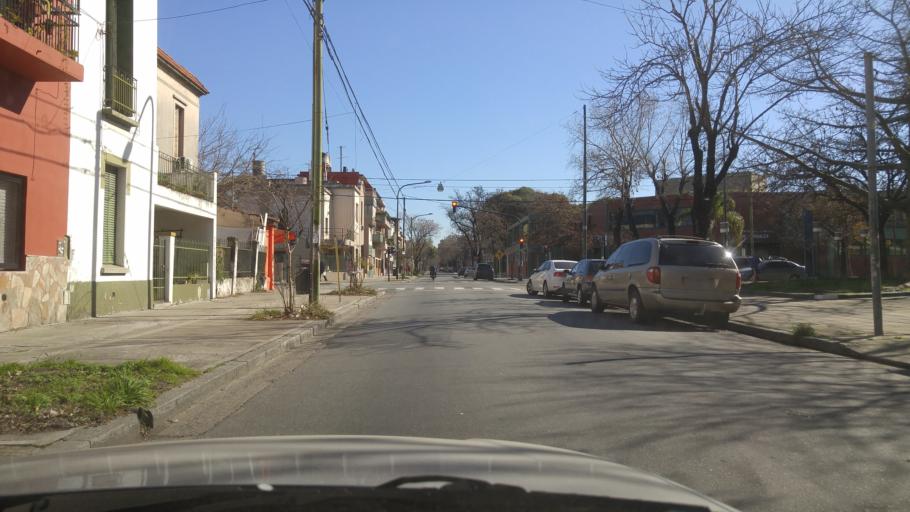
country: AR
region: Buenos Aires F.D.
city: Villa Santa Rita
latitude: -34.6219
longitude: -58.4918
